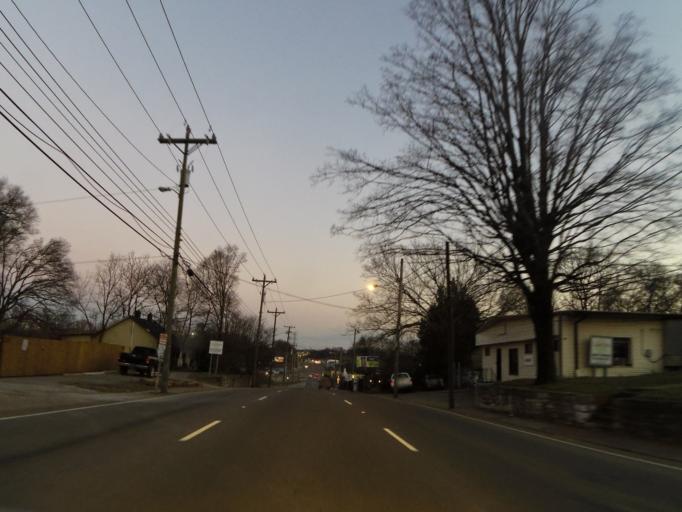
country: US
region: Tennessee
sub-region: Davidson County
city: Nashville
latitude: 36.1384
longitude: -86.7623
